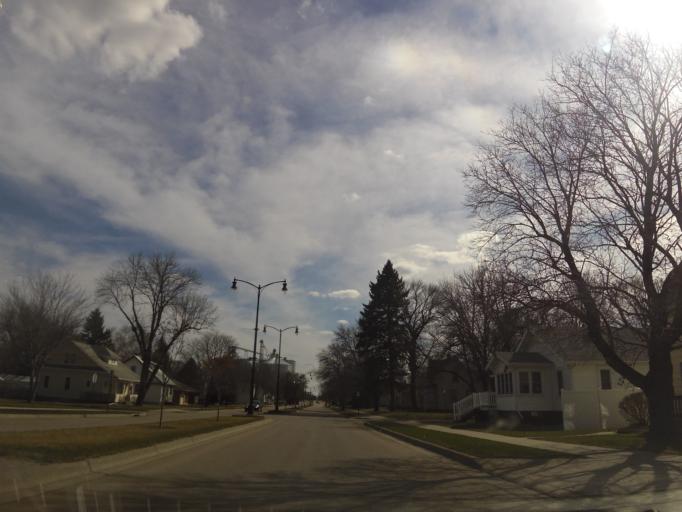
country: US
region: Minnesota
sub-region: Lac qui Parle County
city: Dawson
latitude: 44.9353
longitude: -96.0546
